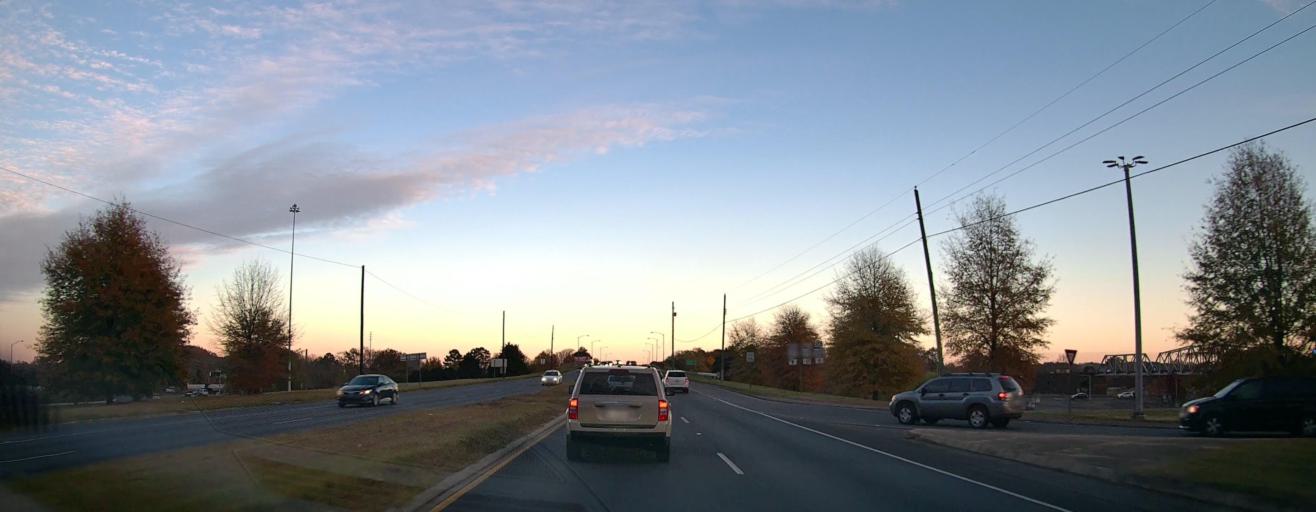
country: US
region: Alabama
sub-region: Etowah County
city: Gadsden
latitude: 34.0141
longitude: -85.9982
